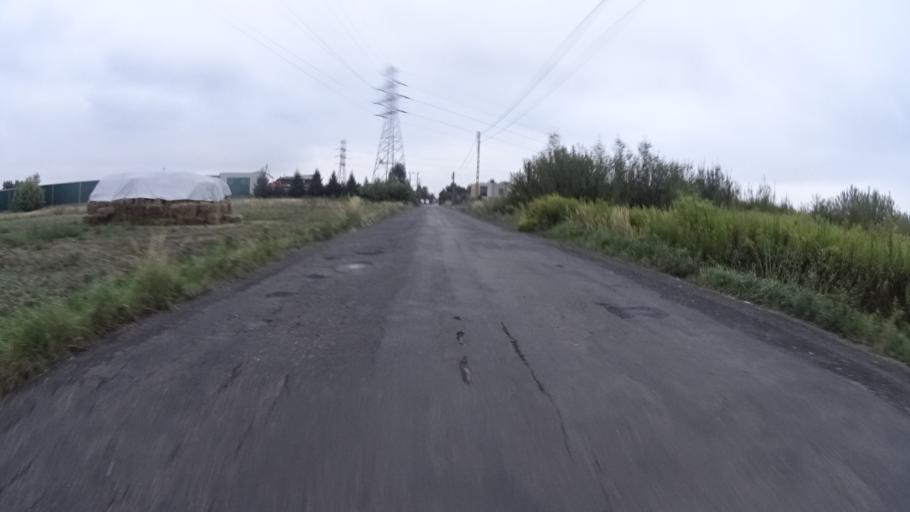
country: PL
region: Masovian Voivodeship
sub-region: Warszawa
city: Ursus
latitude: 52.2211
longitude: 20.8782
